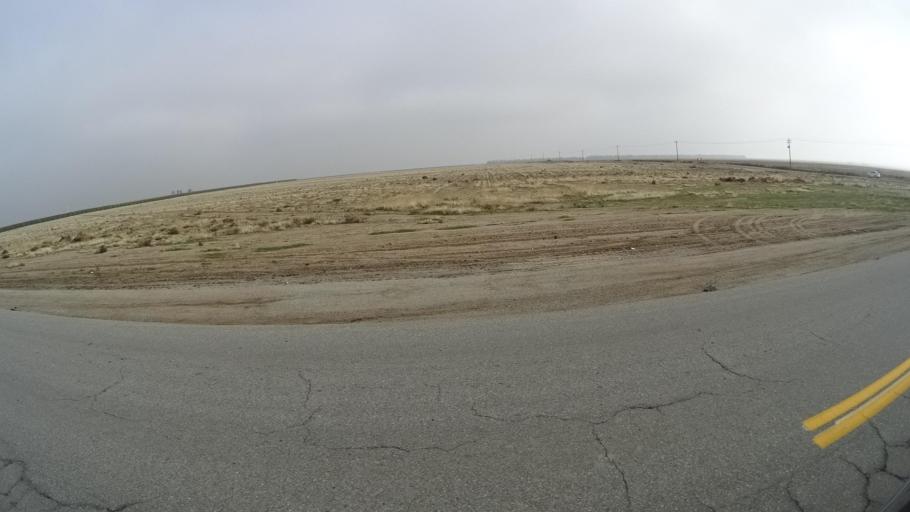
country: US
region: California
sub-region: Kern County
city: Maricopa
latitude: 35.0592
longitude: -119.3137
